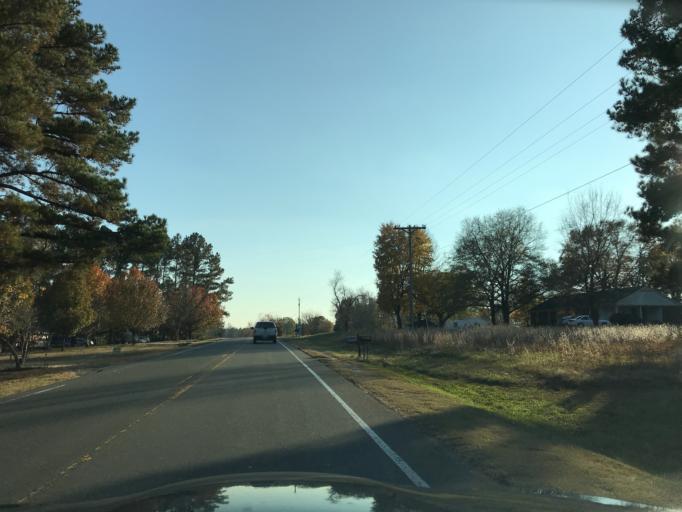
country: US
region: North Carolina
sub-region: Granville County
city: Creedmoor
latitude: 36.0563
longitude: -78.6974
